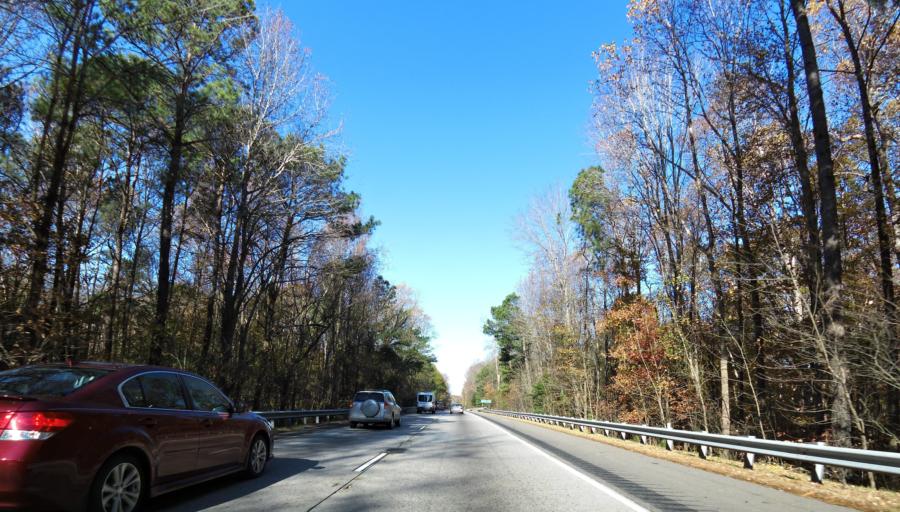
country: US
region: Virginia
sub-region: City of Williamsburg
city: Williamsburg
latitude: 37.2770
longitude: -76.6613
